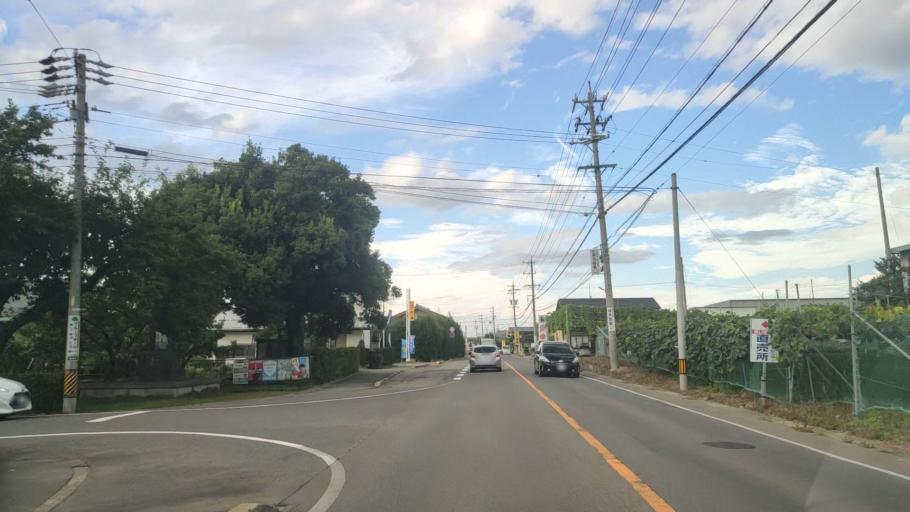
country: JP
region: Nagano
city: Suzaka
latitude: 36.6729
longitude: 138.3163
